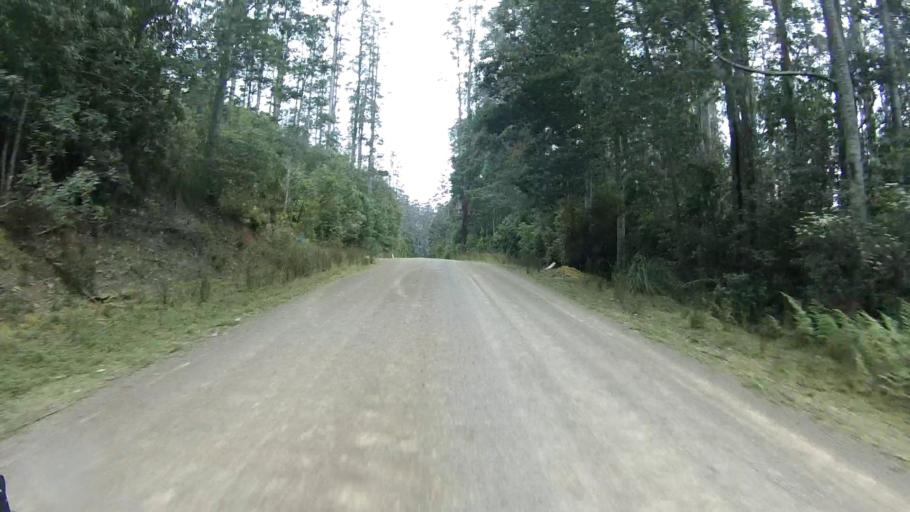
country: AU
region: Tasmania
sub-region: Sorell
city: Sorell
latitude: -42.7151
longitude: 147.8416
